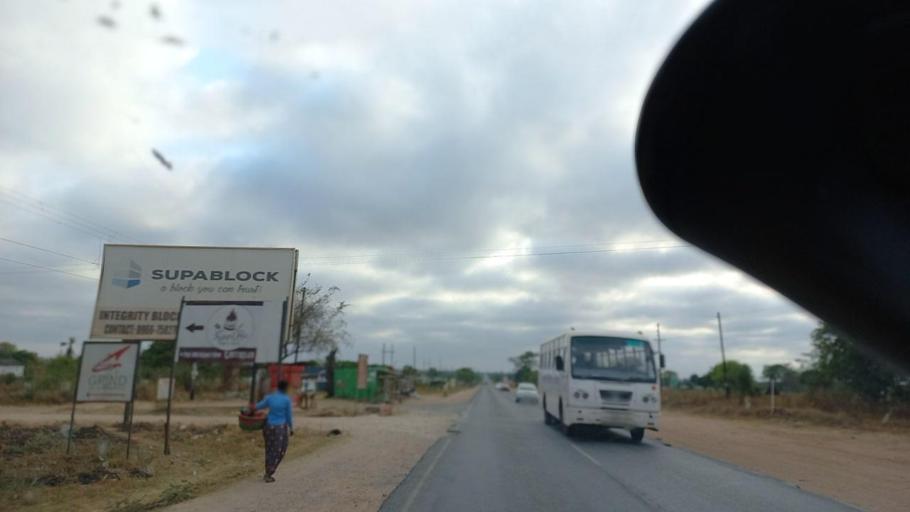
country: ZM
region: Lusaka
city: Chongwe
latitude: -15.3545
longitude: 28.4846
